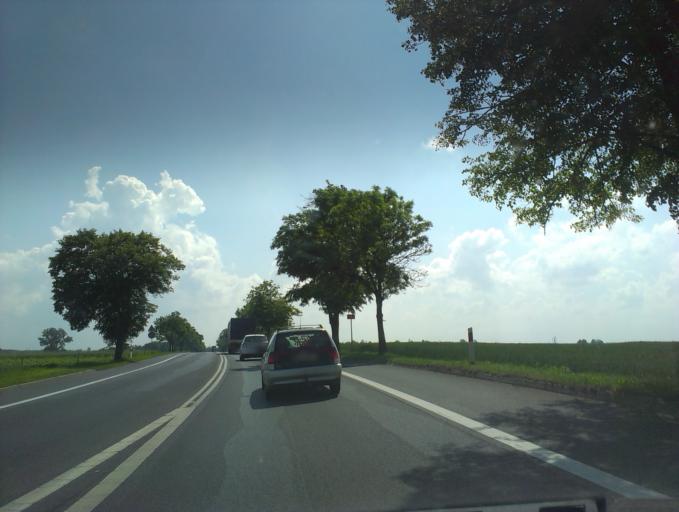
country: PL
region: Greater Poland Voivodeship
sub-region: Powiat pilski
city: Ujscie
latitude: 53.0454
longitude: 16.7511
